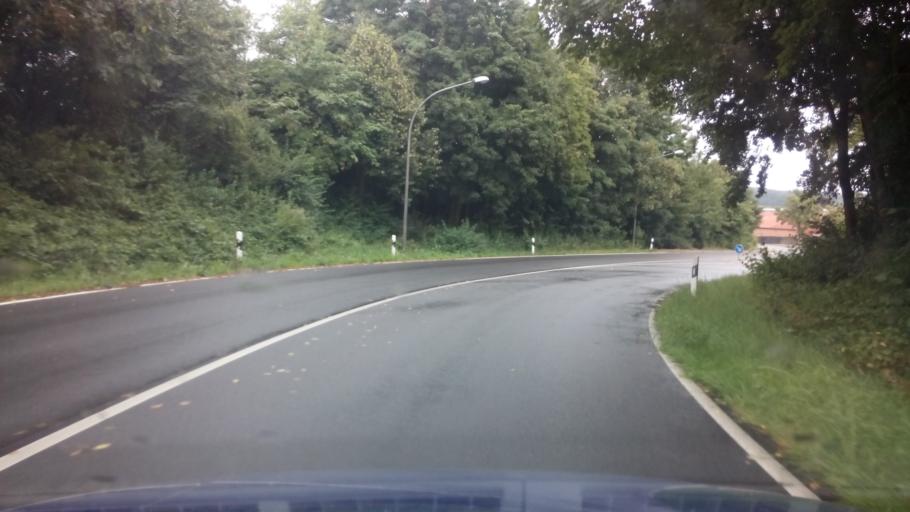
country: DE
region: Lower Saxony
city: Melle
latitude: 52.2405
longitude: 8.3168
